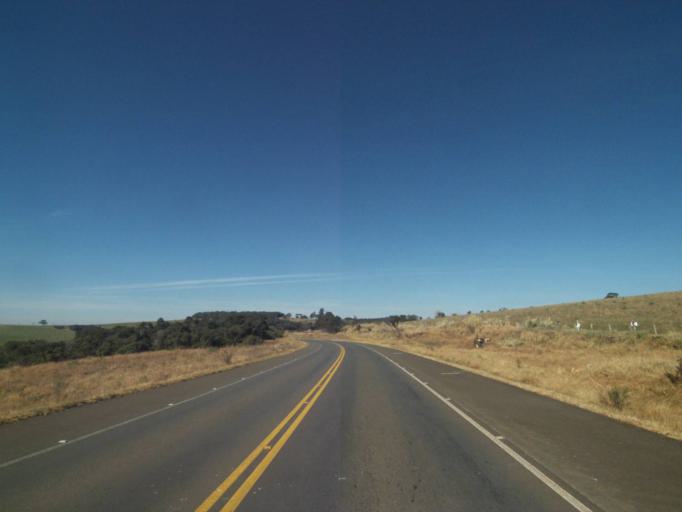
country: BR
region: Parana
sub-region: Tibagi
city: Tibagi
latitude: -24.7700
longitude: -50.4670
